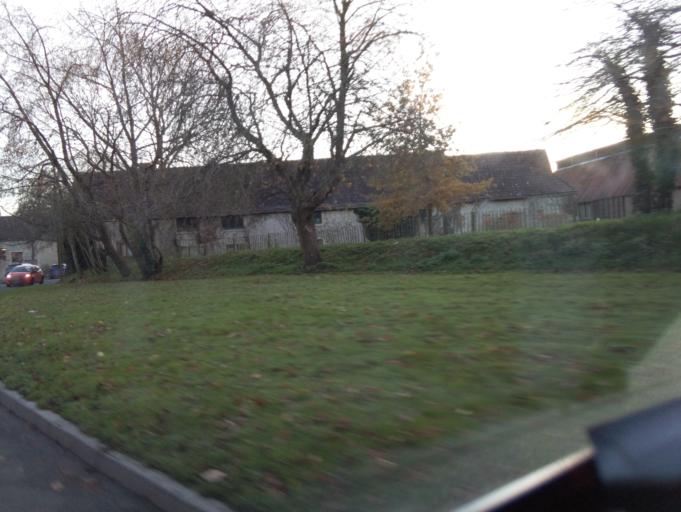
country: GB
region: England
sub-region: Wiltshire
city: Warminster
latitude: 51.2077
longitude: -2.1884
